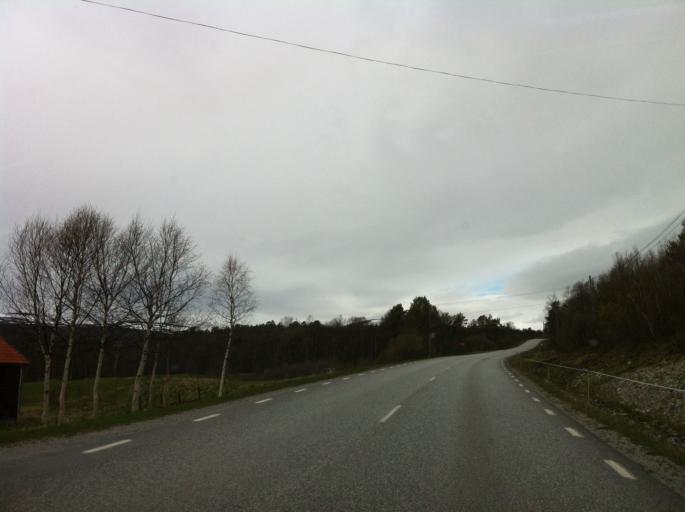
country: NO
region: Sor-Trondelag
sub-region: Tydal
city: Aas
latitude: 62.6205
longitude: 12.4733
